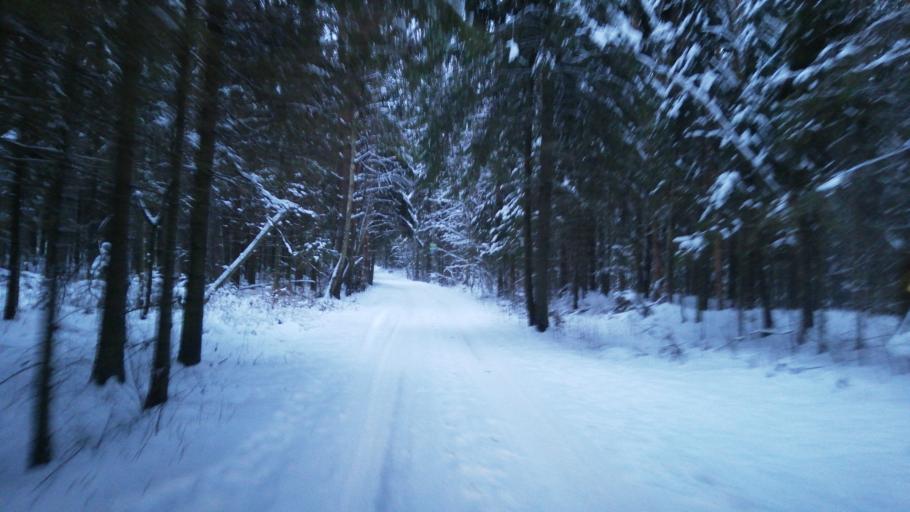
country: RU
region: Jaroslavl
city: Krasnyye Tkachi
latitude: 57.4492
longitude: 39.7942
